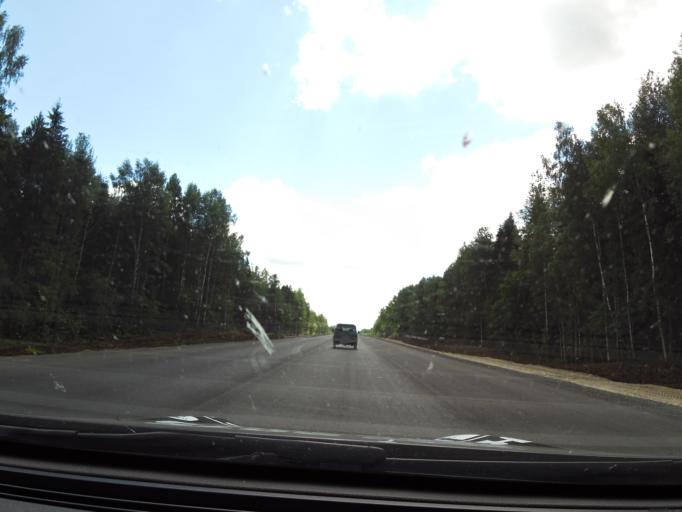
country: RU
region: Vologda
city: Molochnoye
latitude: 59.3316
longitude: 39.6815
